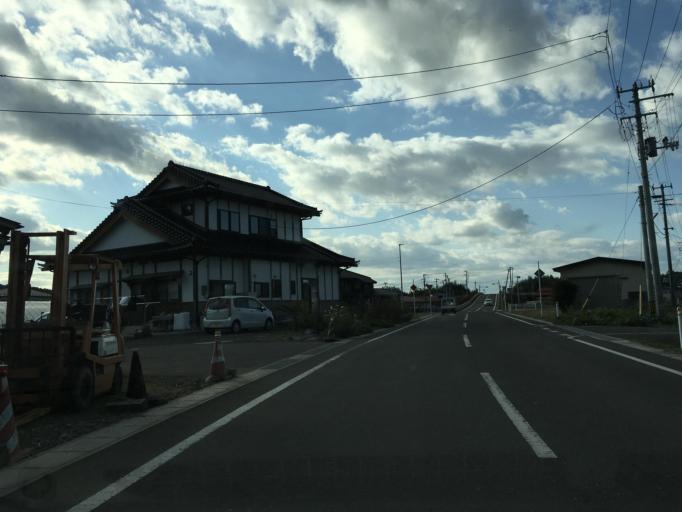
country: JP
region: Miyagi
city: Wakuya
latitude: 38.6517
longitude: 141.2910
